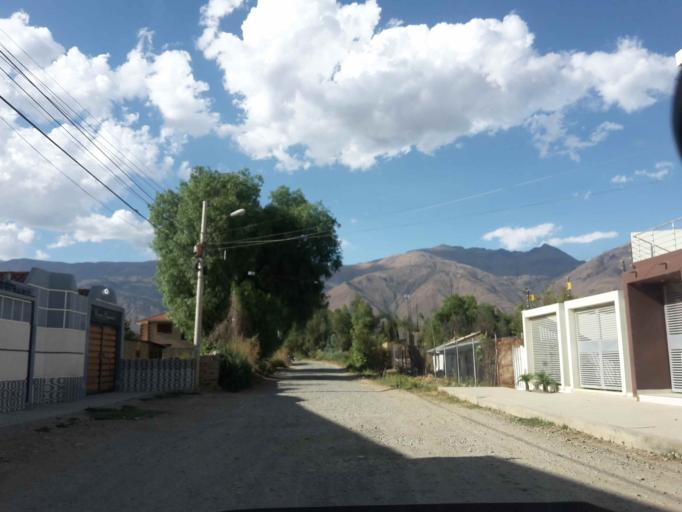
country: BO
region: Cochabamba
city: Cochabamba
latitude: -17.3671
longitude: -66.2076
